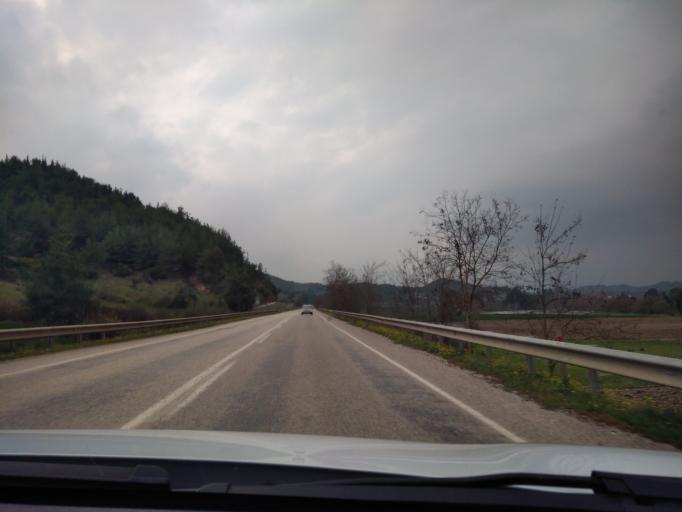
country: TR
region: Mersin
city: Yenice
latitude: 37.0937
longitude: 35.1224
